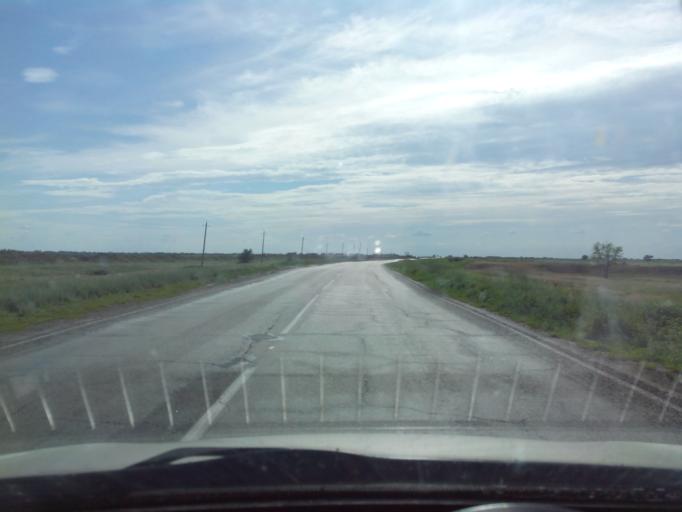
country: RU
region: Astrakhan
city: Znamensk
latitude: 48.5889
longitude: 45.6840
